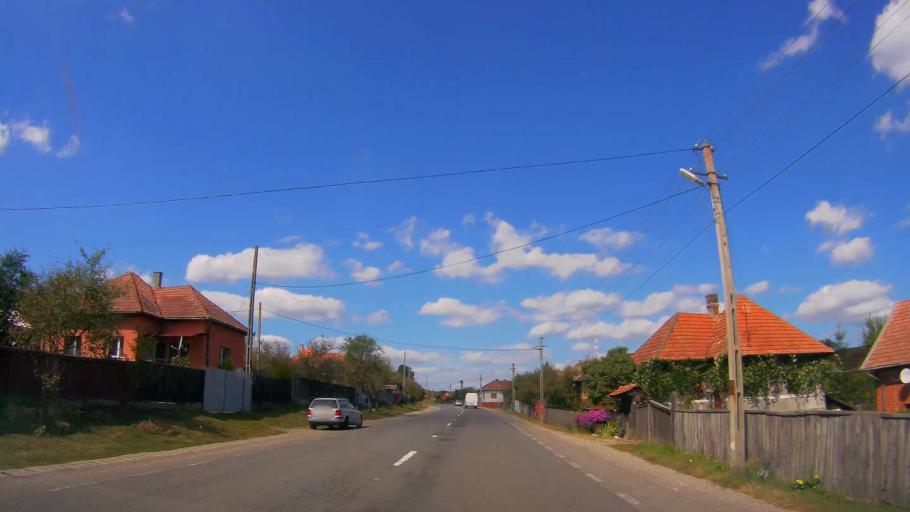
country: RO
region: Cluj
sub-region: Comuna Sanpaul
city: Sanpaul
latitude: 46.9306
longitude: 23.3965
